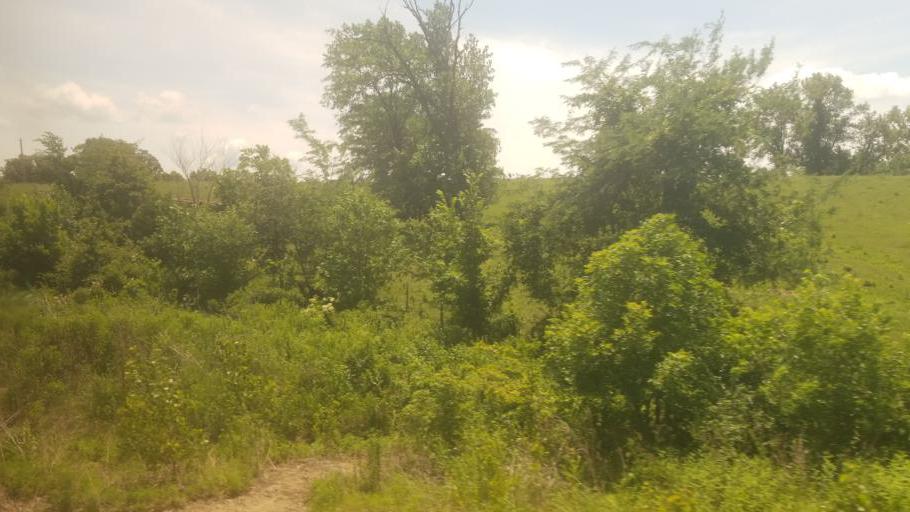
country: US
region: Missouri
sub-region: Linn County
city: Marceline
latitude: 39.8683
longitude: -92.7835
